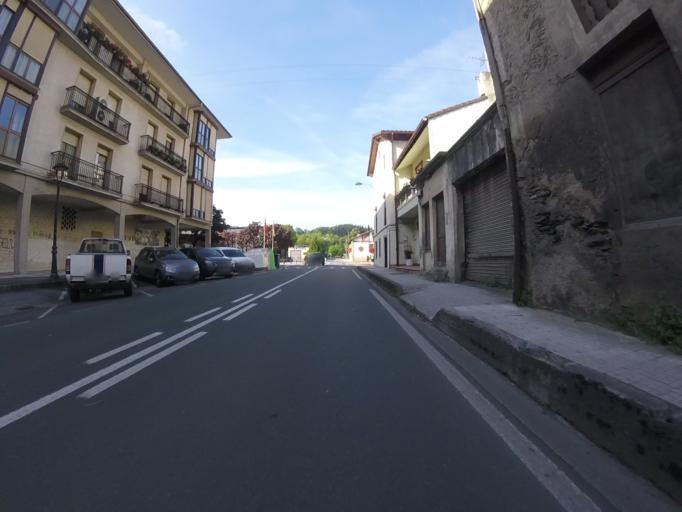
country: ES
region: Basque Country
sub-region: Provincia de Guipuzcoa
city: Isasondo
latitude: 43.0677
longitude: -2.1647
